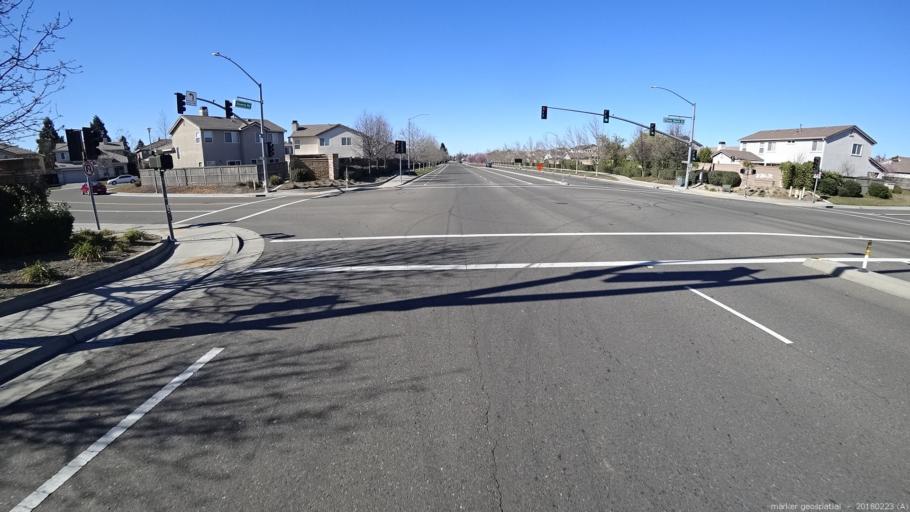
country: US
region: California
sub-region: Sacramento County
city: Antelope
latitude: 38.7077
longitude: -121.3541
